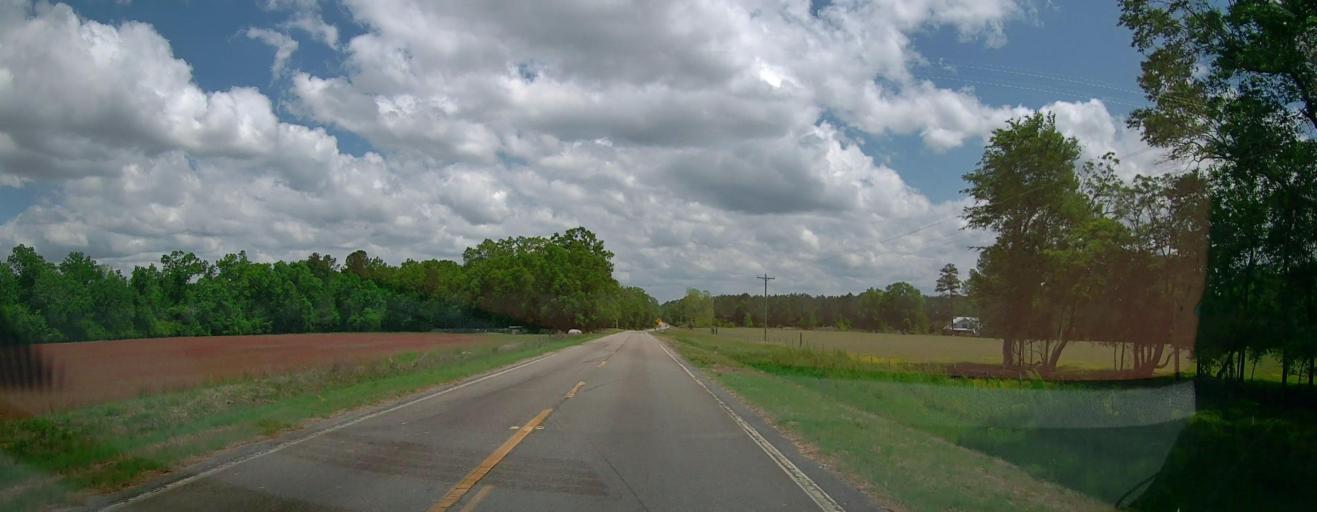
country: US
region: Georgia
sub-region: Dodge County
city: Chester
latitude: 32.5229
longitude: -83.2138
